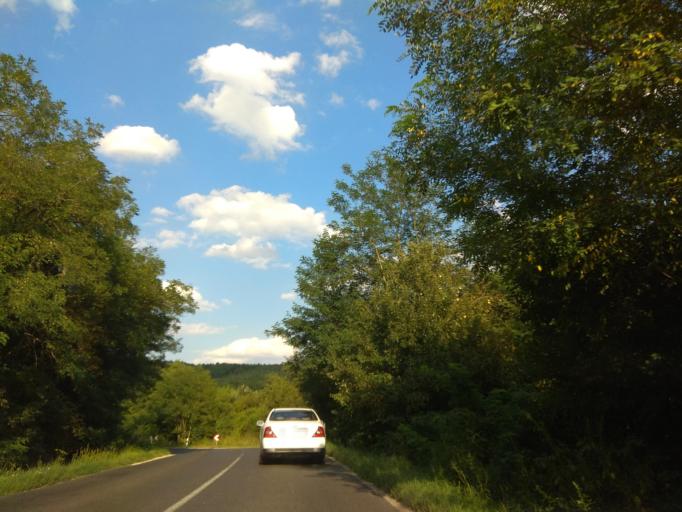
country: HU
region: Borsod-Abauj-Zemplen
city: Harsany
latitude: 47.9966
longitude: 20.7569
